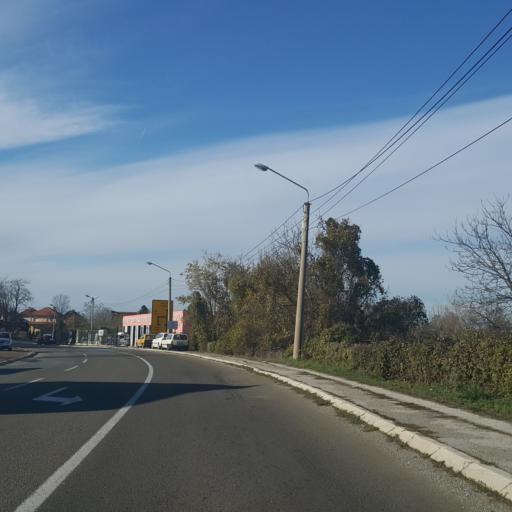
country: RS
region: Central Serbia
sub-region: Sumadijski Okrug
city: Topola
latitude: 44.2557
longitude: 20.6850
